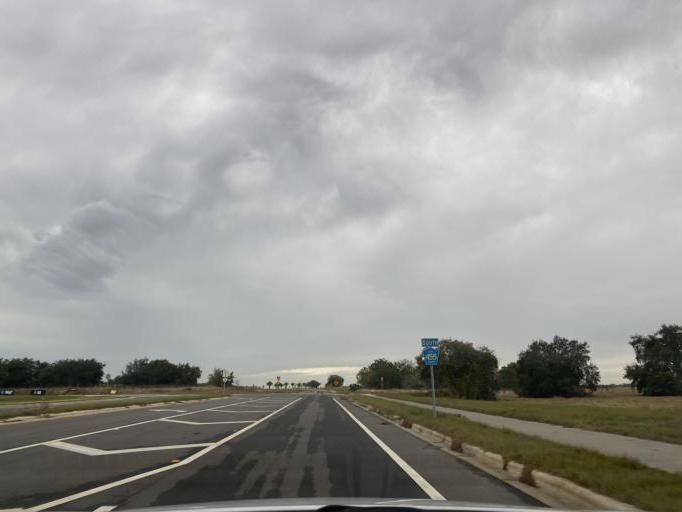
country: US
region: Florida
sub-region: Orange County
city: Oakland
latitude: 28.5394
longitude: -81.6863
